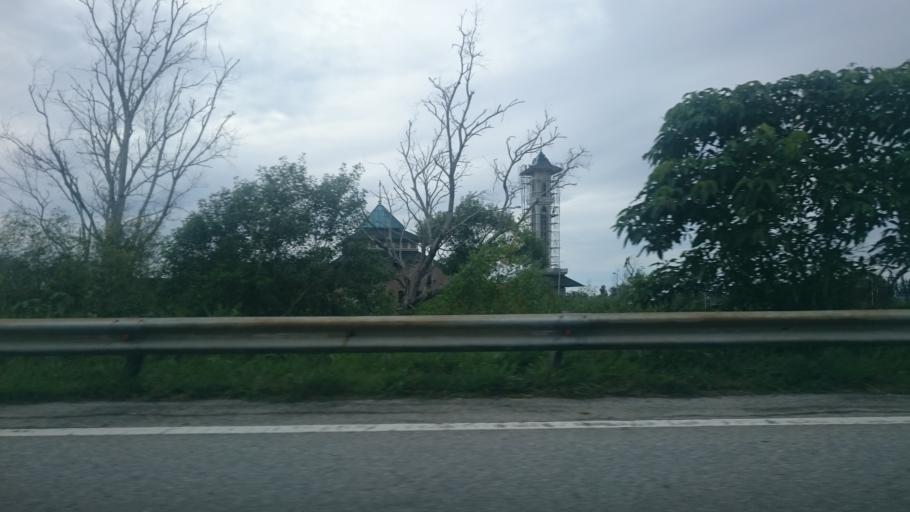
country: BN
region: Tutong
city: Tutong
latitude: 4.8131
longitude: 114.6504
